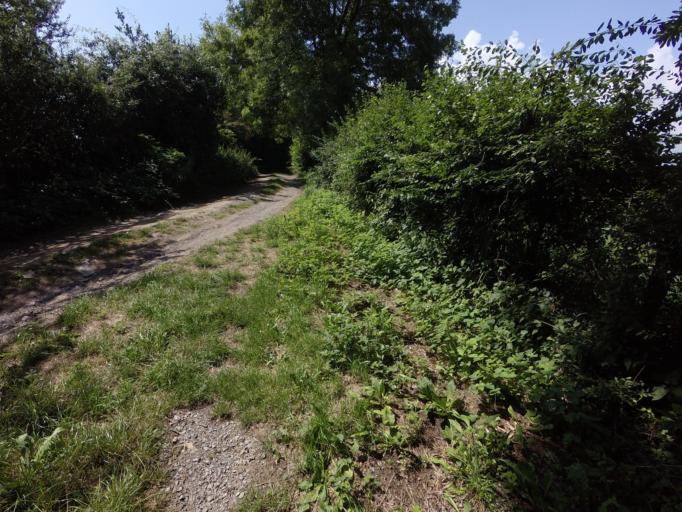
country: BE
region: Wallonia
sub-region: Province de Liege
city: Lontzen
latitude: 50.6953
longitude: 5.9903
